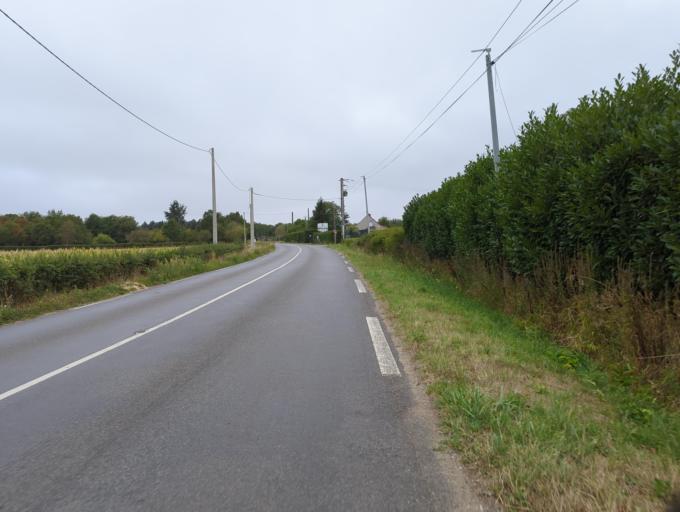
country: FR
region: Pays de la Loire
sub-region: Departement de Maine-et-Loire
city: Trelaze
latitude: 47.4705
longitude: -0.4602
